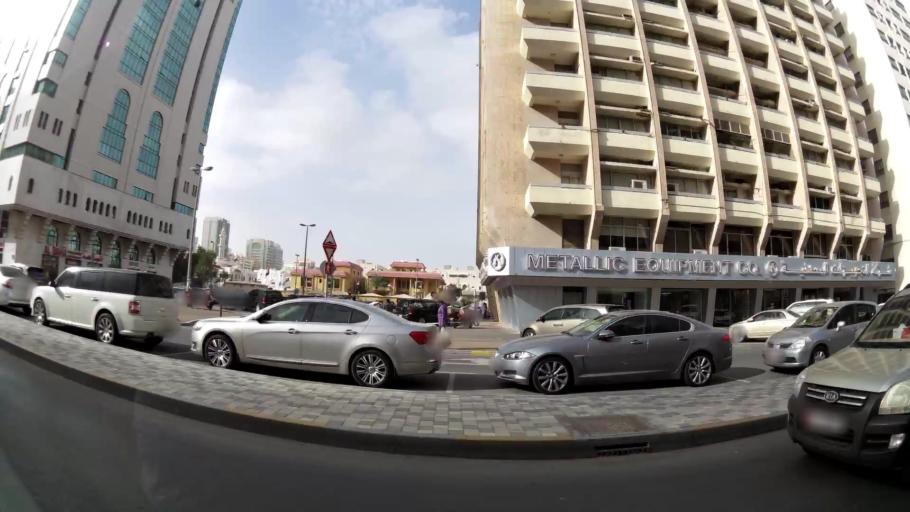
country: AE
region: Abu Dhabi
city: Abu Dhabi
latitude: 24.4848
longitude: 54.3740
